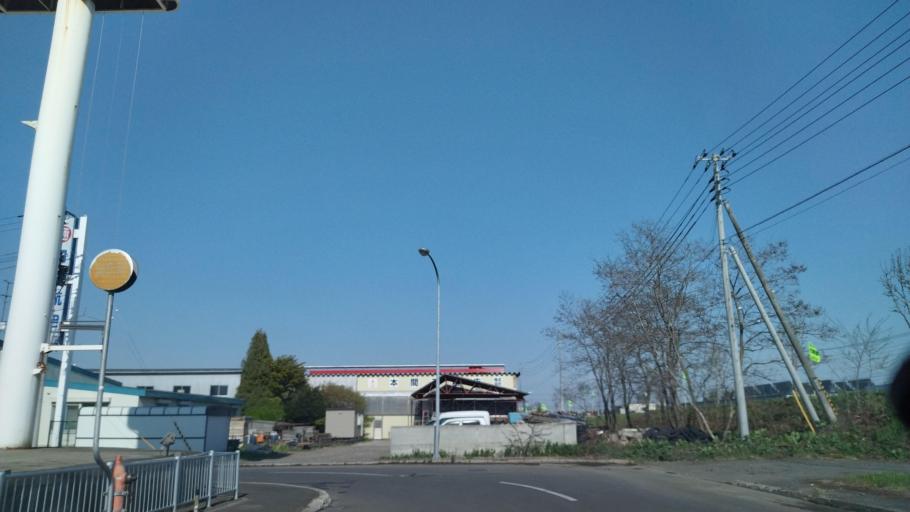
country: JP
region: Hokkaido
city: Obihiro
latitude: 42.9239
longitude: 143.0859
